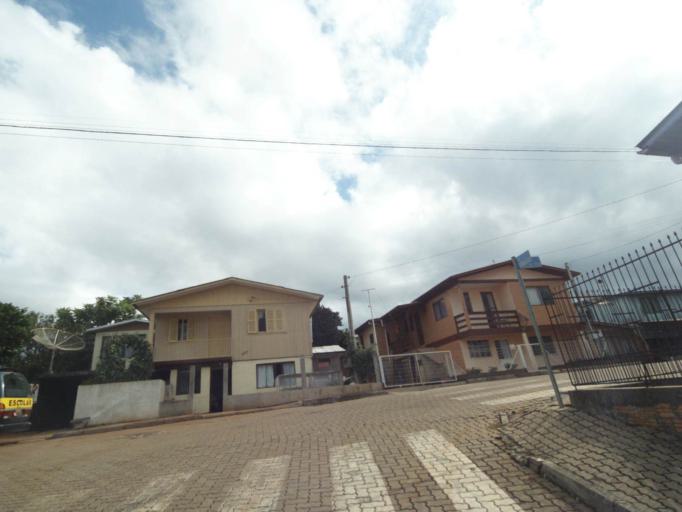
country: BR
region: Rio Grande do Sul
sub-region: Lagoa Vermelha
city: Lagoa Vermelha
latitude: -28.1992
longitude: -51.5262
